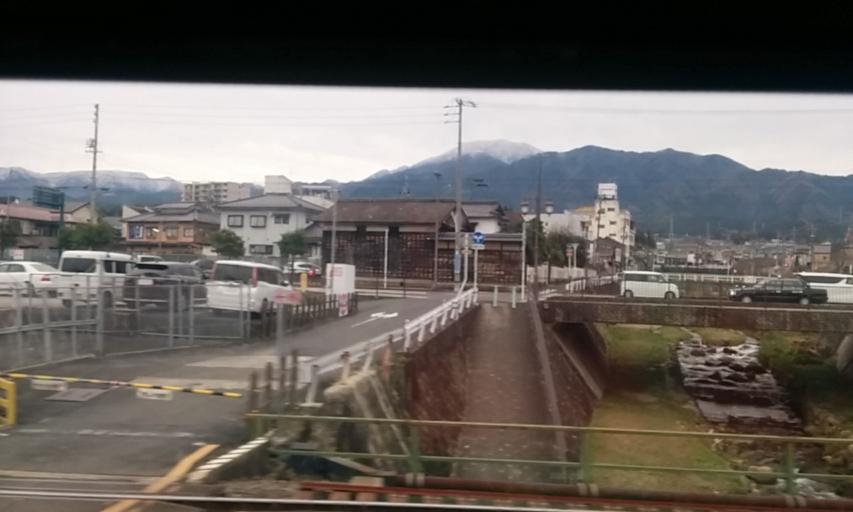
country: JP
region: Gifu
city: Nakatsugawa
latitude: 35.4979
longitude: 137.5016
